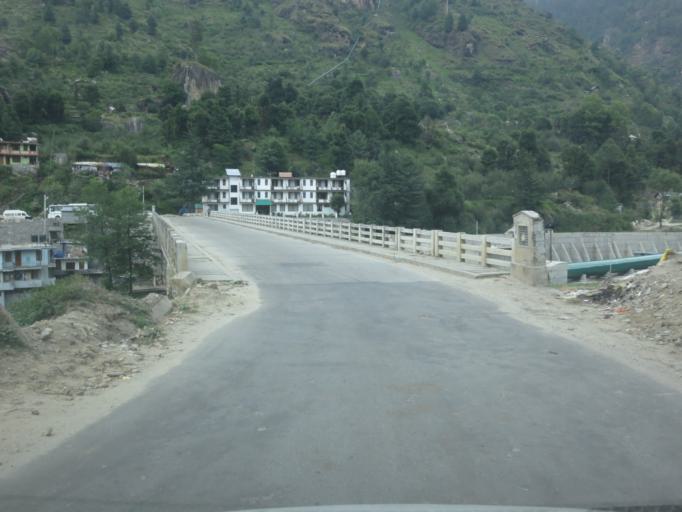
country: IN
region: Himachal Pradesh
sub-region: Kulu
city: Manali
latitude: 32.2256
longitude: 77.1976
